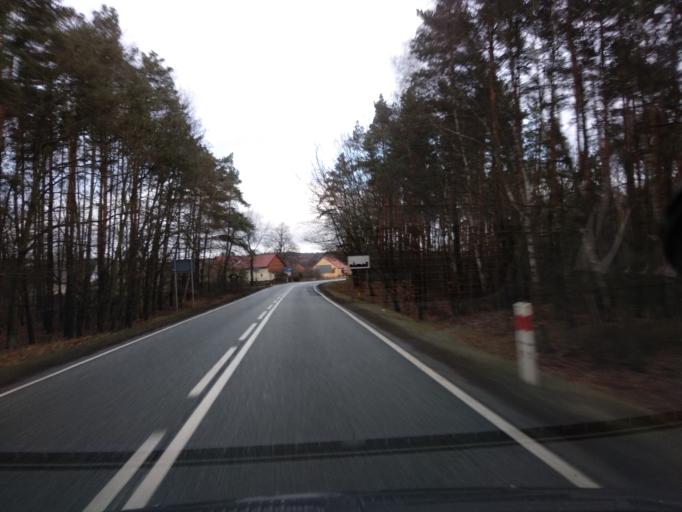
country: PL
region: Lower Silesian Voivodeship
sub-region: Powiat olesnicki
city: Miedzyborz
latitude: 51.3679
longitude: 17.6139
